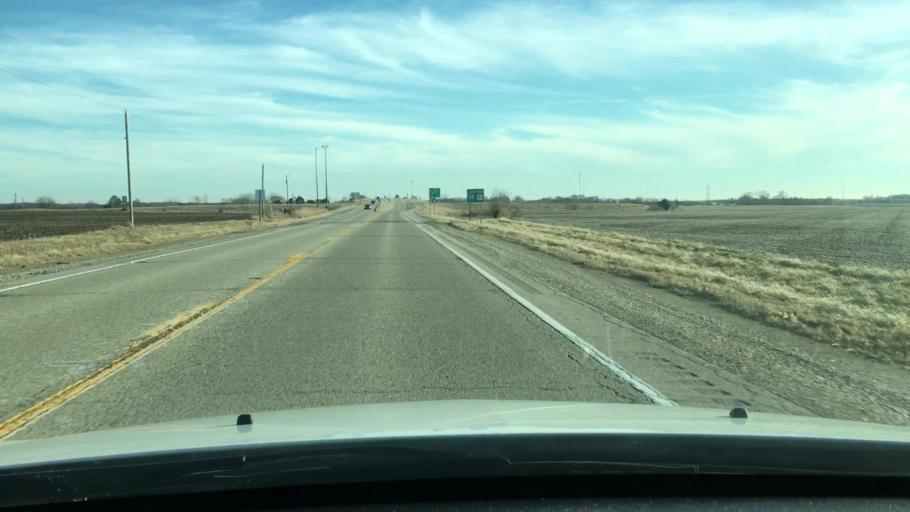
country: US
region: Illinois
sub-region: LaSalle County
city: Oglesby
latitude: 41.2803
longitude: -89.0861
